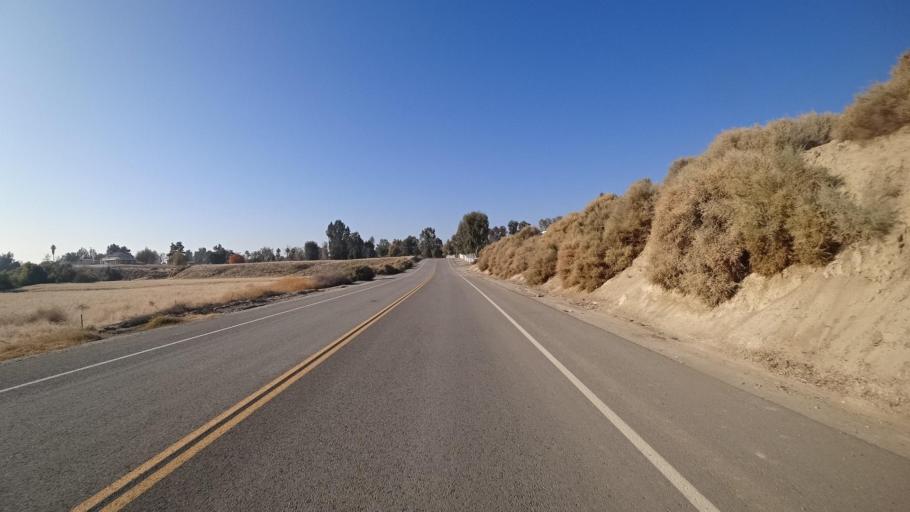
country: US
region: California
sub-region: Kern County
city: Oildale
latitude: 35.4527
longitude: -118.9066
